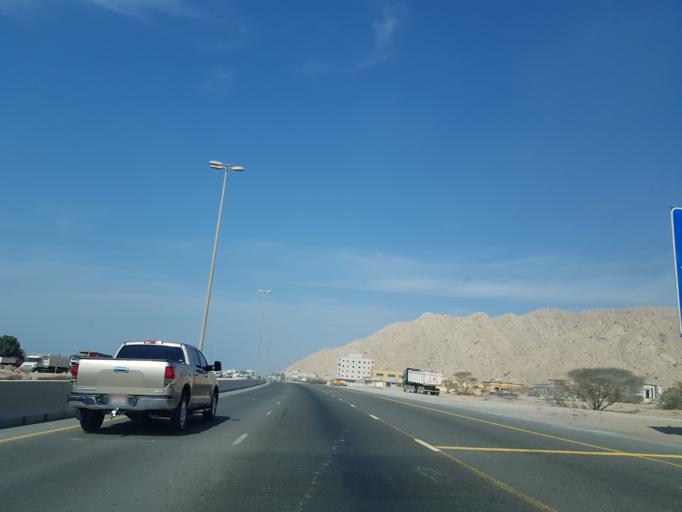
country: AE
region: Ra's al Khaymah
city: Ras al-Khaimah
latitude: 25.8459
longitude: 56.0196
